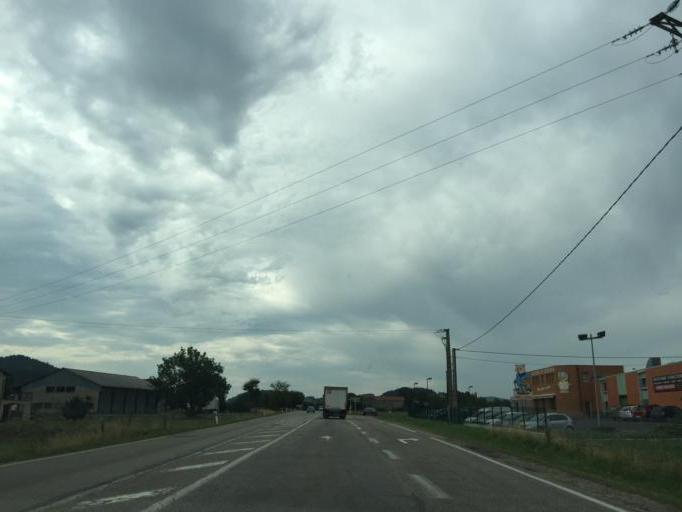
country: FR
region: Auvergne
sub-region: Departement de la Haute-Loire
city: Solignac-sur-Loire
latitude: 44.9642
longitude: 3.8447
